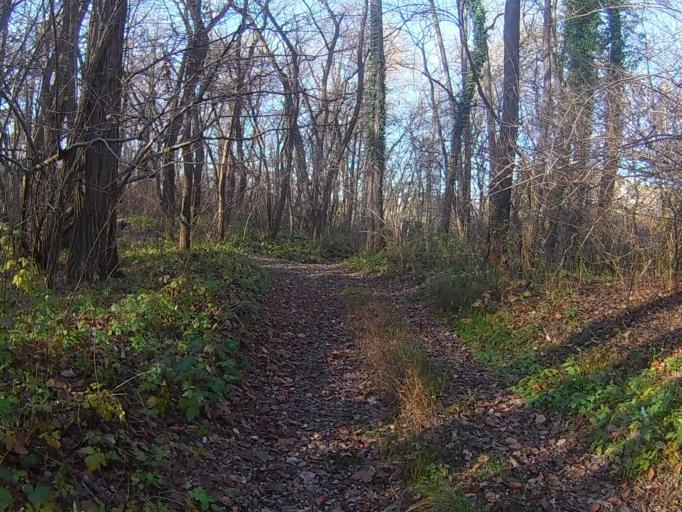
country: SI
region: Duplek
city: Zgornji Duplek
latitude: 46.5102
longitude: 15.7201
